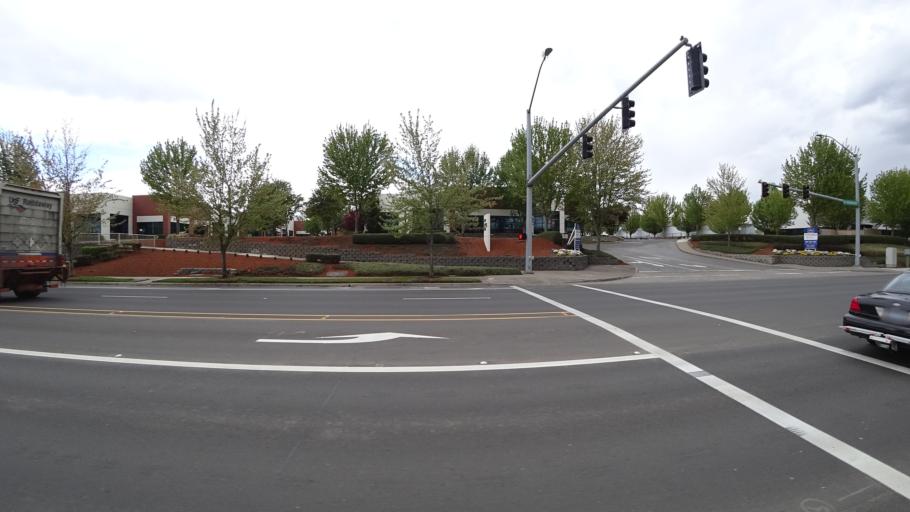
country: US
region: Oregon
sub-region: Washington County
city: Rockcreek
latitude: 45.5508
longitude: -122.9147
